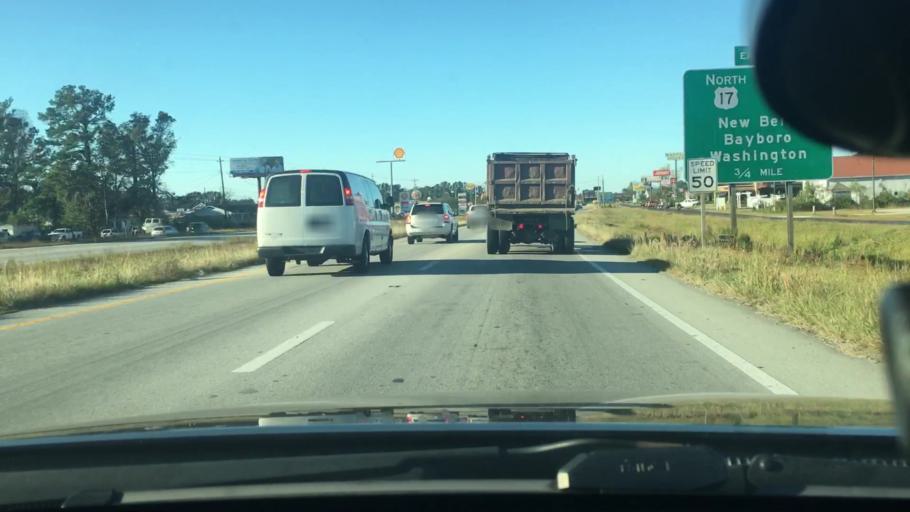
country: US
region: North Carolina
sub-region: Craven County
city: James City
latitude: 35.0793
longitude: -77.0301
